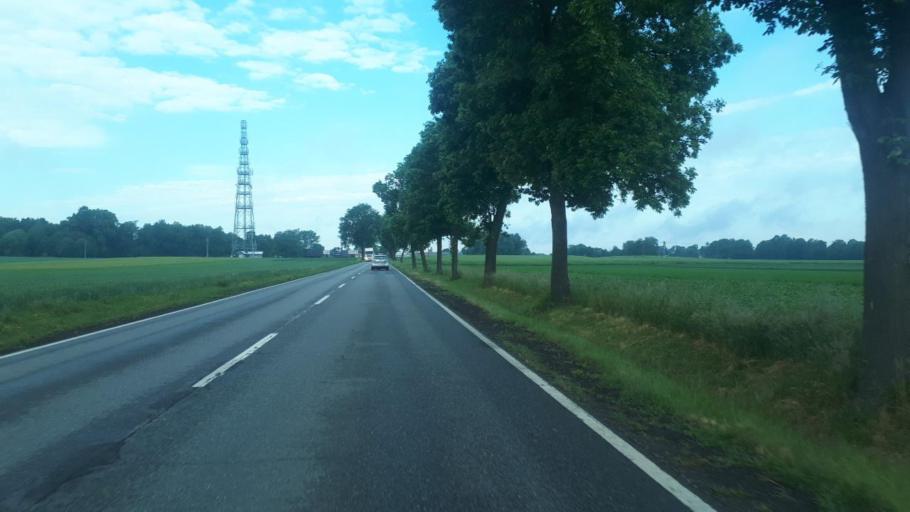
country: PL
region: Silesian Voivodeship
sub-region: Powiat pszczynski
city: Miedzna
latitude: 49.9698
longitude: 19.0627
